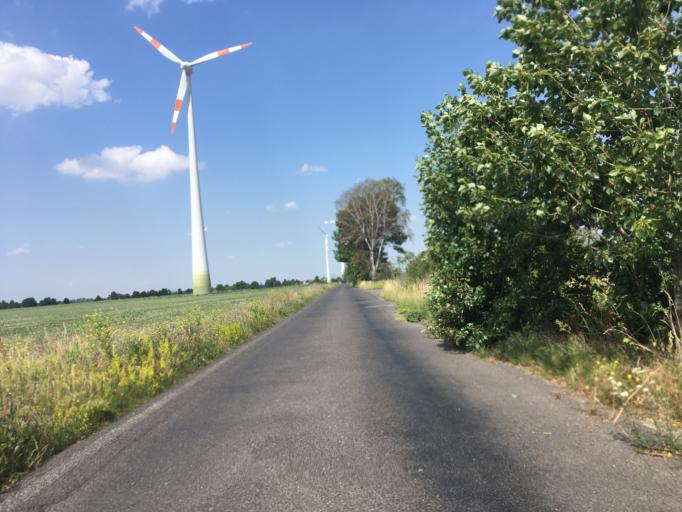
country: DE
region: Saxony-Anhalt
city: Quellendorf
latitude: 51.7850
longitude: 12.1306
